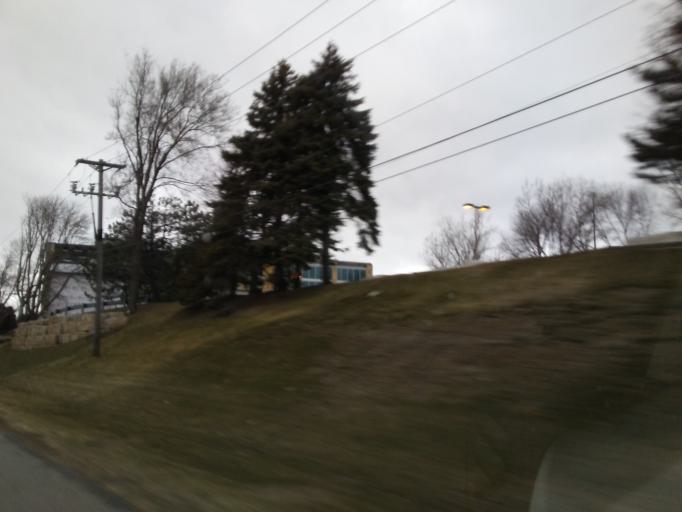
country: US
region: Minnesota
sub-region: Hennepin County
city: Eden Prairie
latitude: 44.8586
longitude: -93.4167
